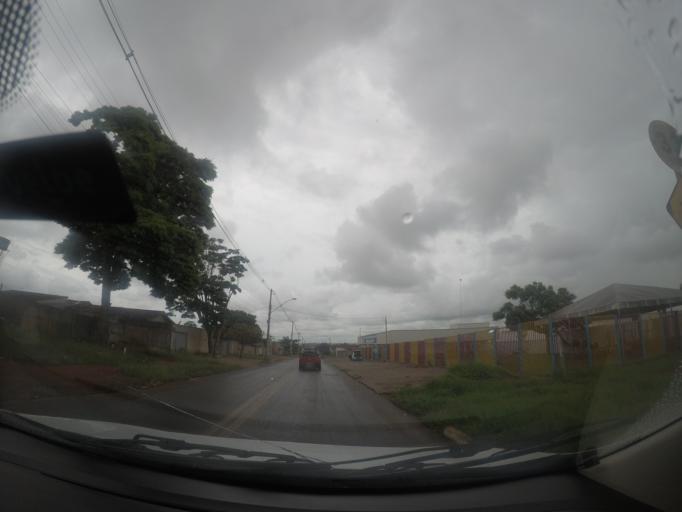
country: BR
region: Goias
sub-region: Trindade
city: Trindade
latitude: -16.6387
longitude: -49.3881
